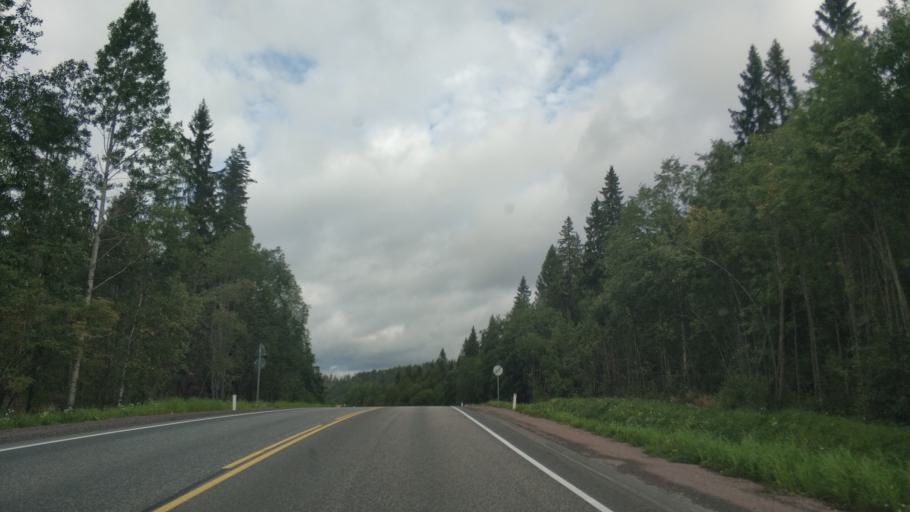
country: RU
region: Republic of Karelia
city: Khelyulya
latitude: 61.7947
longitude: 30.6231
